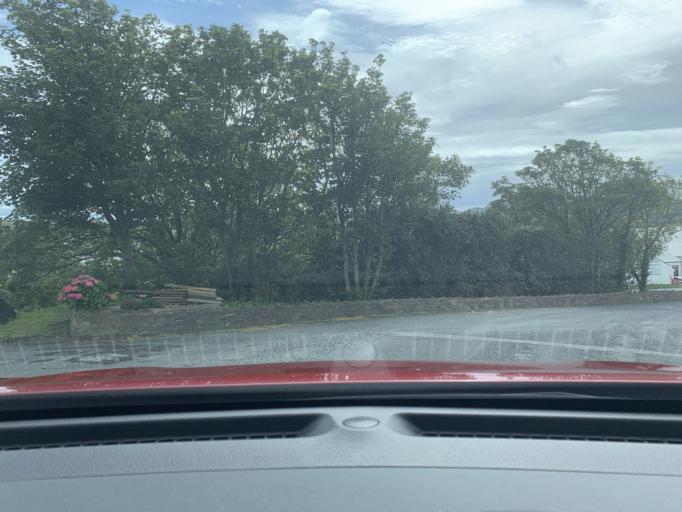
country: IE
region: Ulster
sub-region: County Donegal
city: Dungloe
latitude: 54.9523
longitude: -8.3632
